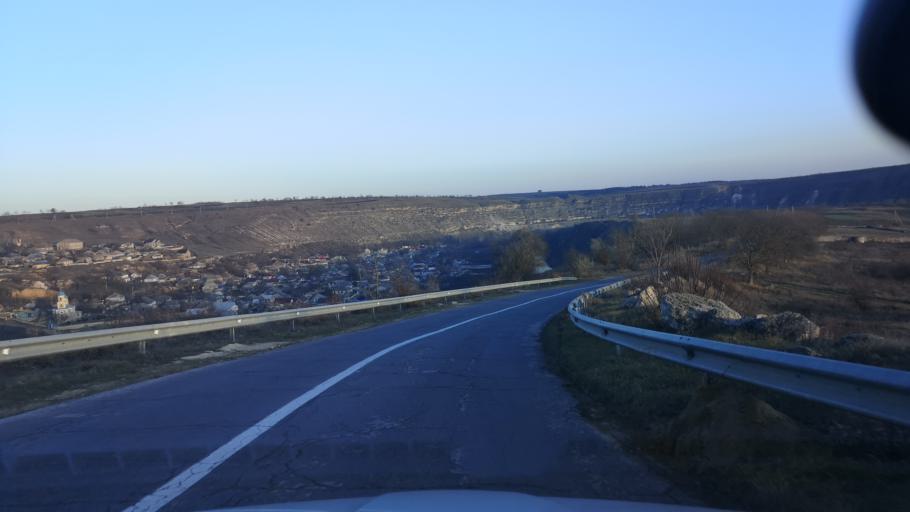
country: MD
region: Telenesti
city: Cocieri
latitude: 47.3106
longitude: 28.9703
